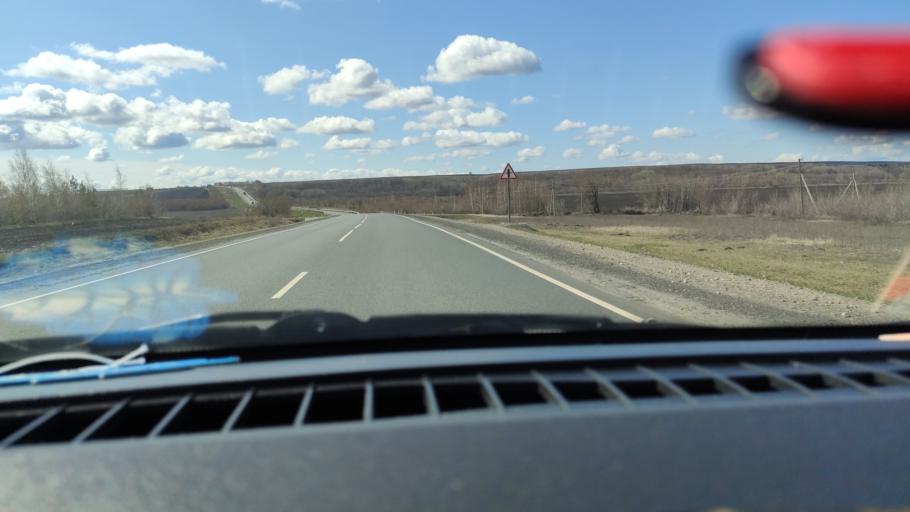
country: RU
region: Samara
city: Syzran'
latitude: 52.9715
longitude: 48.3084
